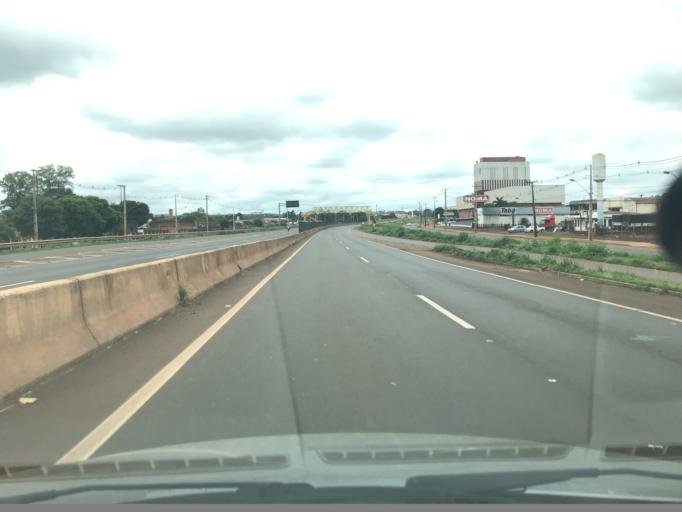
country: BR
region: Parana
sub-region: Paicandu
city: Paicandu
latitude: -23.4489
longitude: -52.0033
